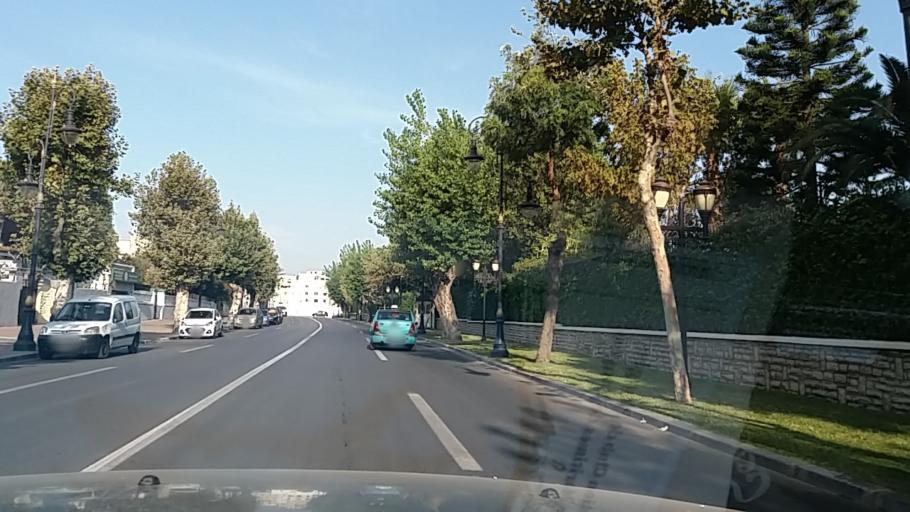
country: MA
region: Tanger-Tetouan
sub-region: Tanger-Assilah
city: Tangier
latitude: 35.7899
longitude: -5.8261
